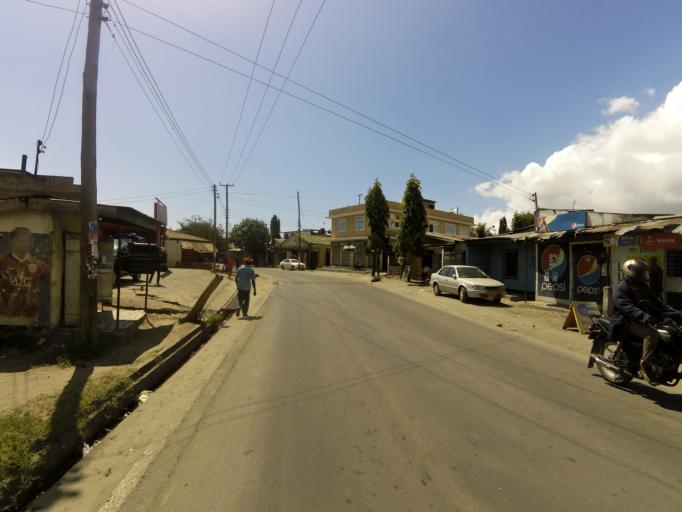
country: TZ
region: Dar es Salaam
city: Magomeni
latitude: -6.8008
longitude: 39.2506
